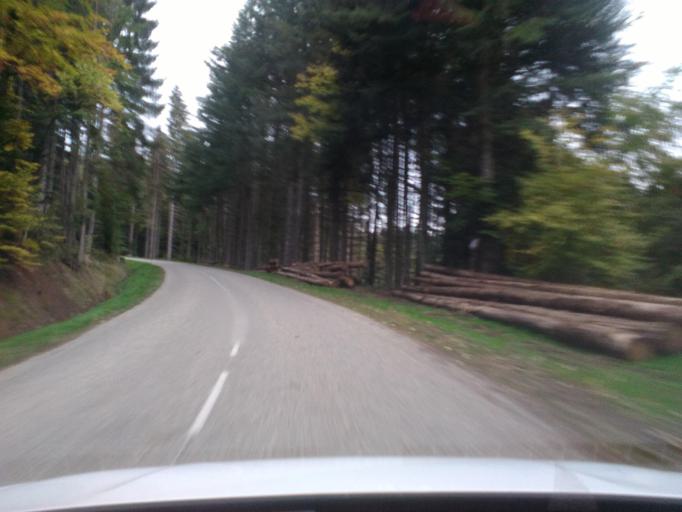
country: FR
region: Lorraine
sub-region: Departement des Vosges
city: Ban-de-Laveline
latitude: 48.3556
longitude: 7.1058
